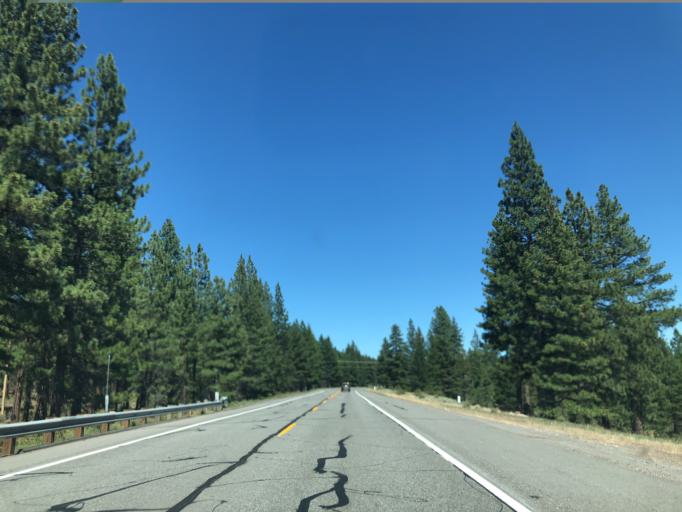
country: US
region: California
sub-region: Lassen County
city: Susanville
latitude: 40.4141
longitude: -120.7423
